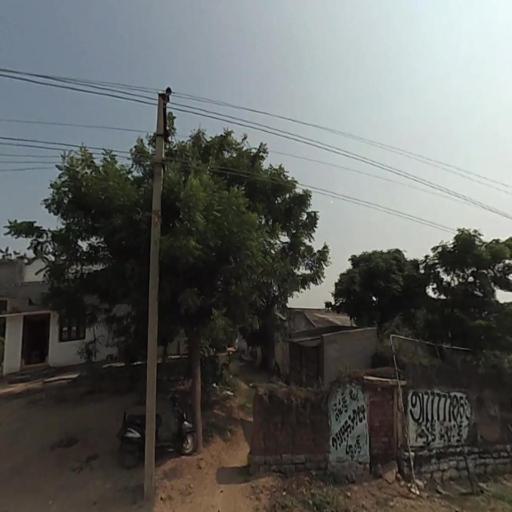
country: IN
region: Telangana
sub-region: Nalgonda
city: Nalgonda
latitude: 17.1888
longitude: 79.1287
